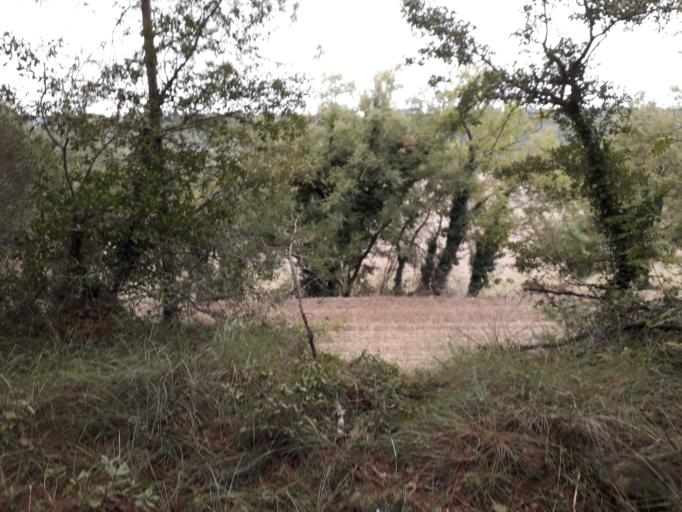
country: ES
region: Catalonia
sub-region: Provincia de Barcelona
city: Bellprat
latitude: 41.5533
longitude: 1.4444
